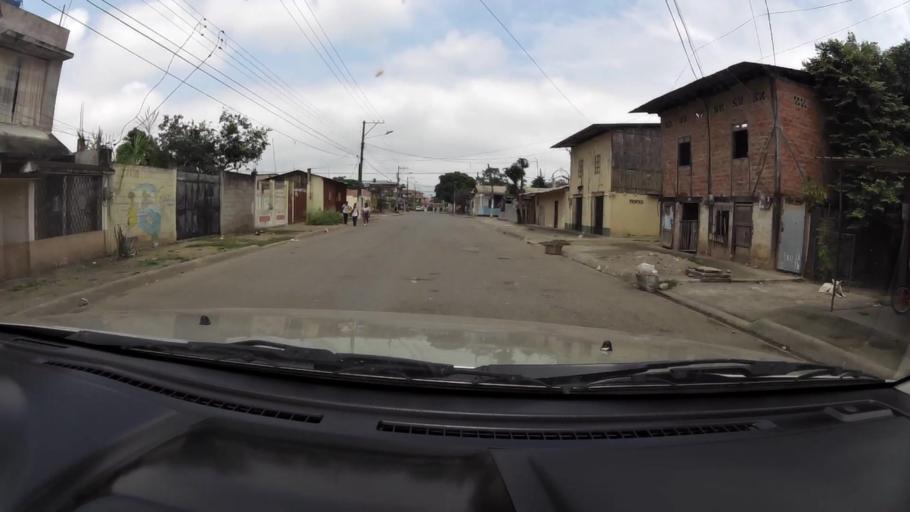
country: EC
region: El Oro
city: Pasaje
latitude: -3.2407
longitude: -79.8268
